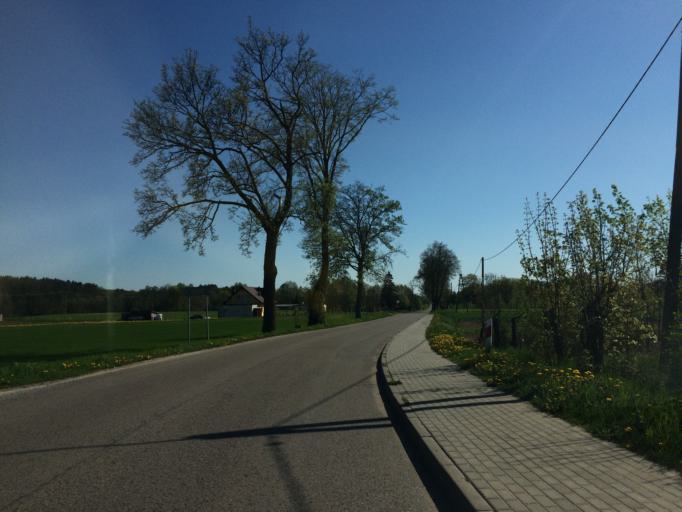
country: PL
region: Warmian-Masurian Voivodeship
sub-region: Powiat ostrodzki
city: Dabrowno
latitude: 53.4979
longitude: 19.9777
